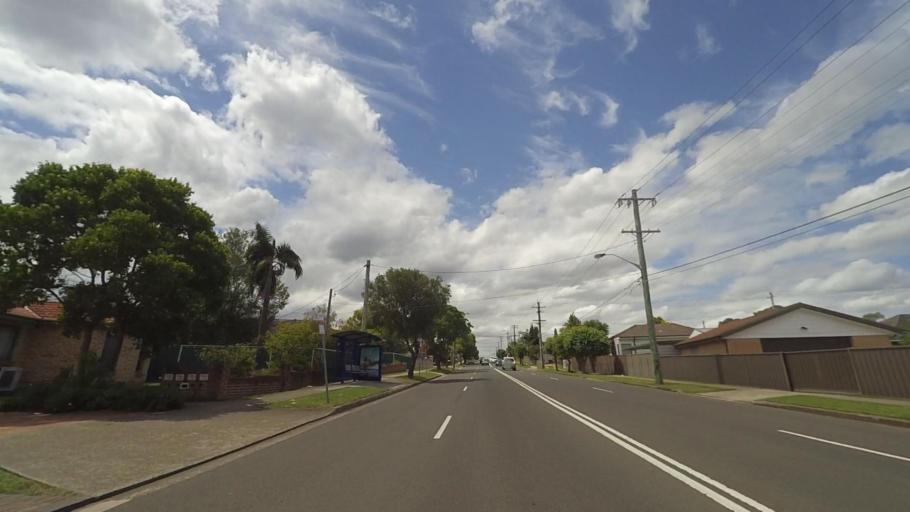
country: AU
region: New South Wales
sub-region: Fairfield
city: Fairfield Heights
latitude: -33.8772
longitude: 150.9427
